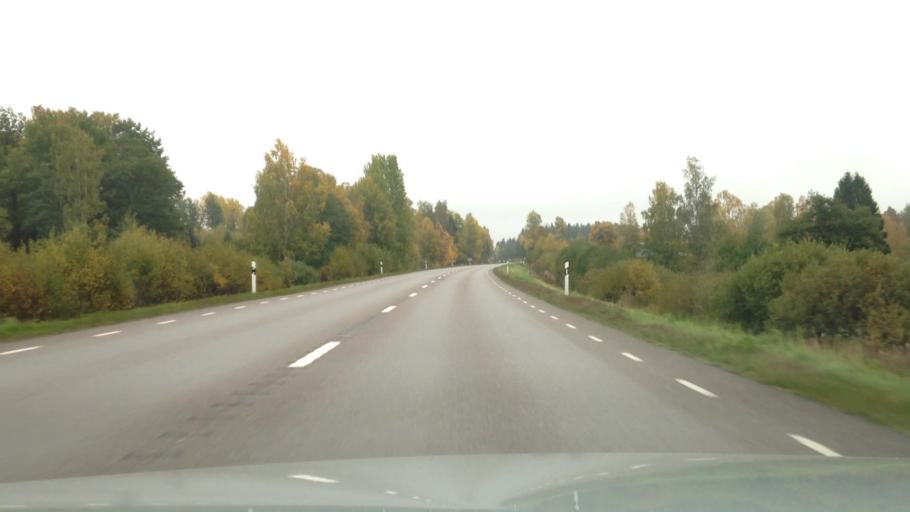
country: SE
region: Vaestra Goetaland
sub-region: Falkopings Kommun
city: Falkoeping
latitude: 58.2660
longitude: 13.4952
